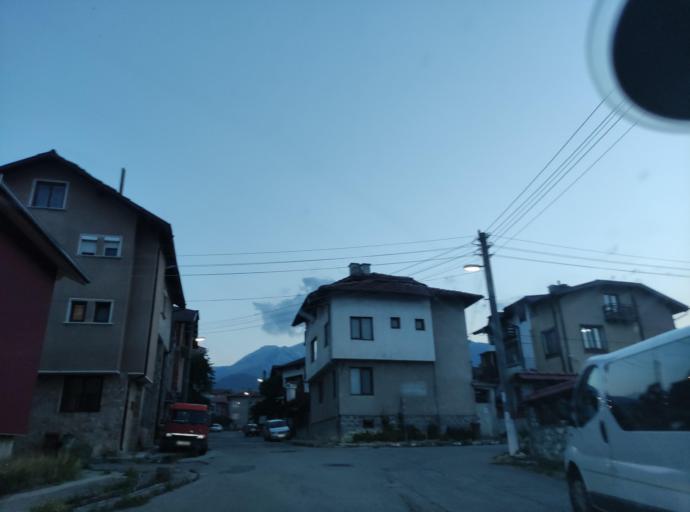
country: BG
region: Blagoevgrad
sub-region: Obshtina Bansko
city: Bansko
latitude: 41.8302
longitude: 23.4869
